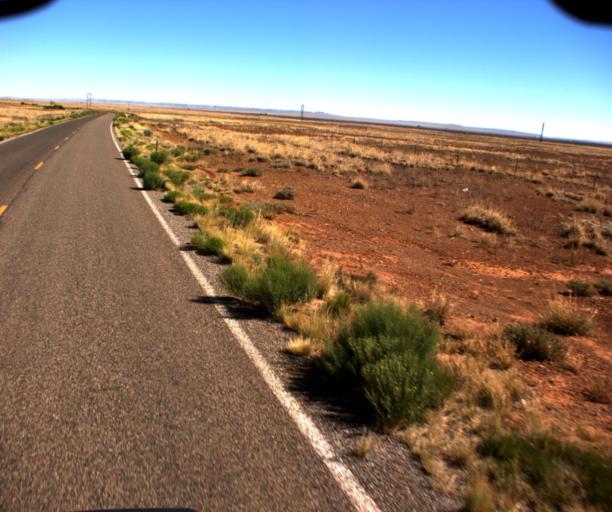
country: US
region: Arizona
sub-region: Coconino County
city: LeChee
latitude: 35.2479
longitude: -110.9611
